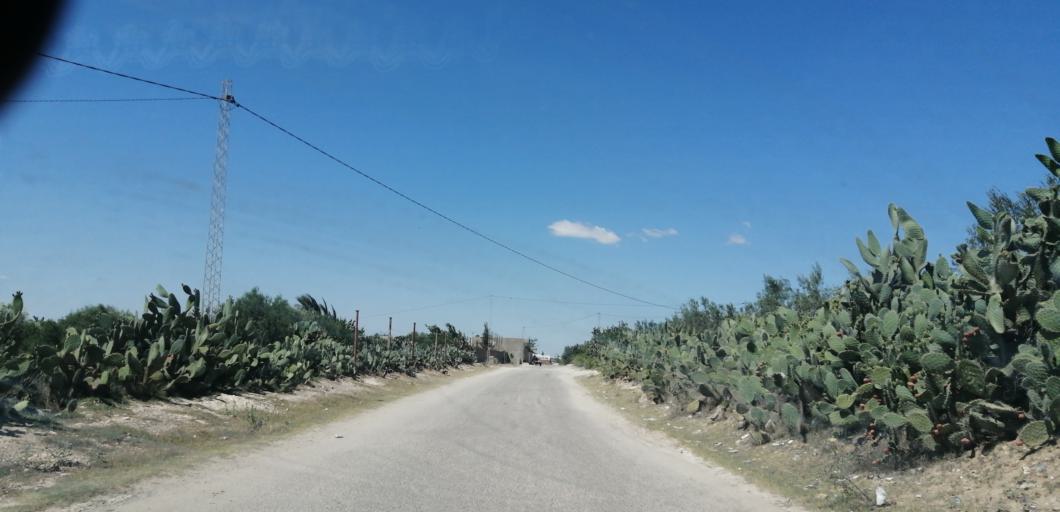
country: TN
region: Al Qayrawan
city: Kairouan
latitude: 35.6286
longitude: 9.9354
